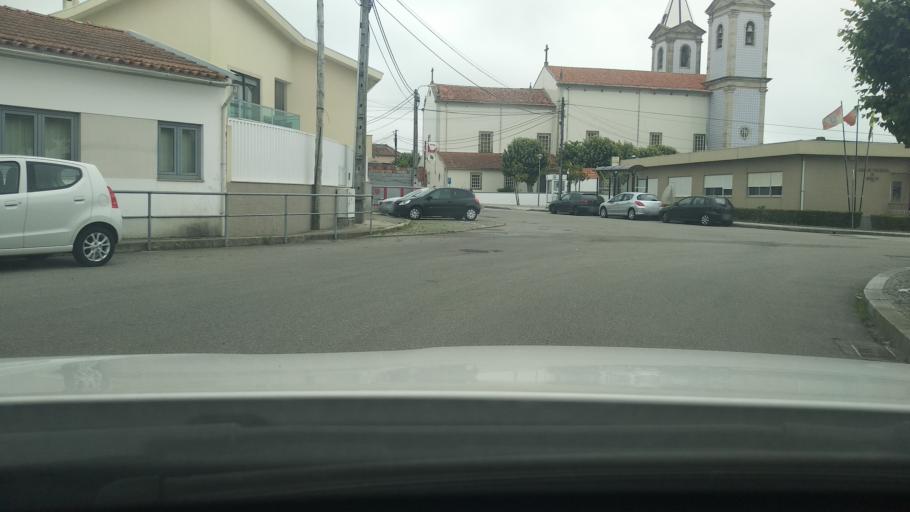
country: PT
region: Aveiro
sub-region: Espinho
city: Silvalde
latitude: 40.9927
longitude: -8.6258
